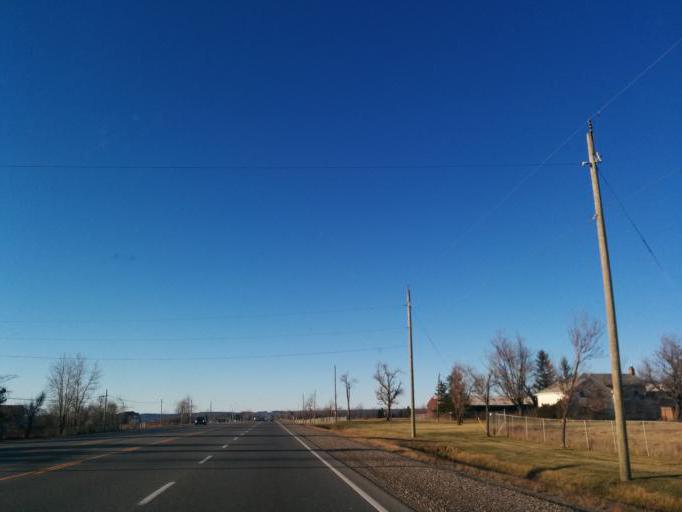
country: CA
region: Ontario
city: Brampton
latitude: 43.7823
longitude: -79.8900
